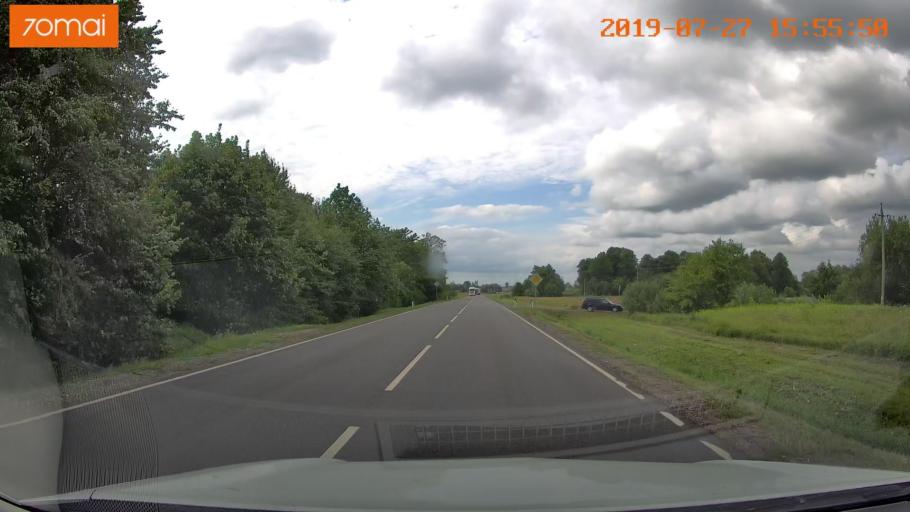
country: RU
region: Kaliningrad
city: Chernyakhovsk
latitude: 54.6152
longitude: 21.9132
